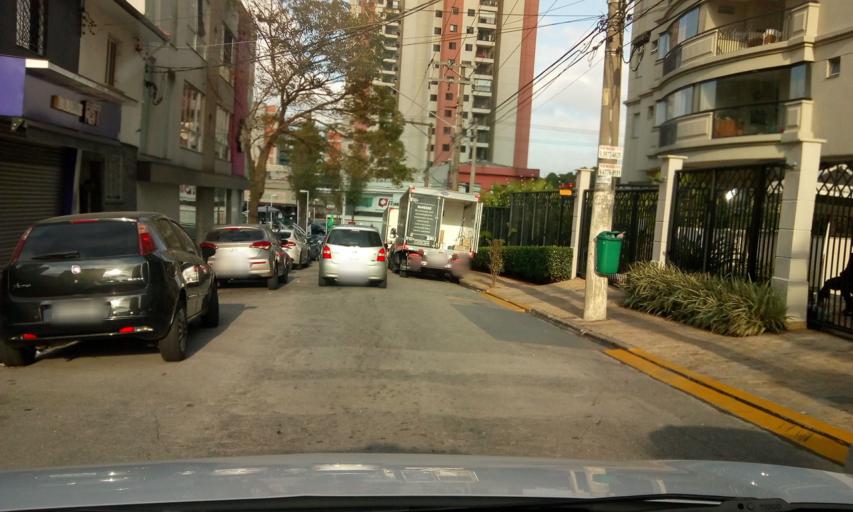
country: BR
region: Sao Paulo
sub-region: Sao Paulo
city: Sao Paulo
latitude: -23.5499
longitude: -46.5950
